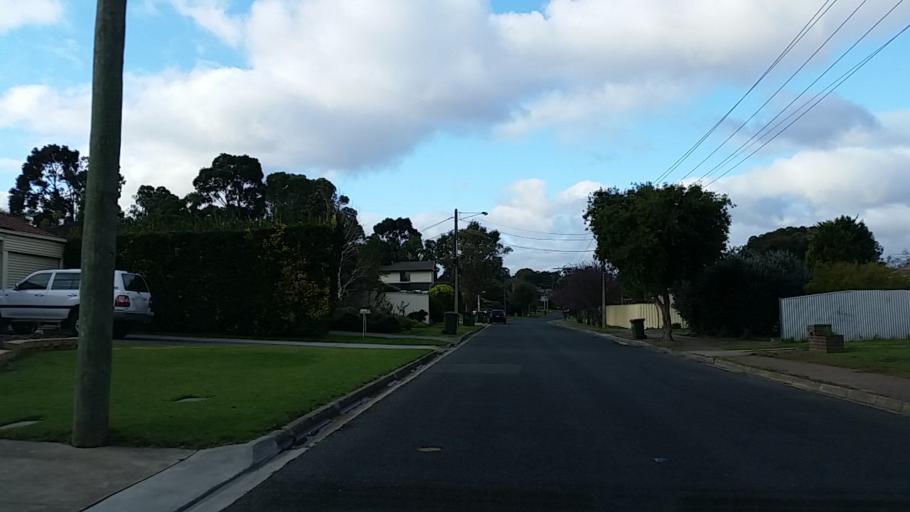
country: AU
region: South Australia
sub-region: Tea Tree Gully
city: Modbury
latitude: -34.8378
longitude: 138.6728
